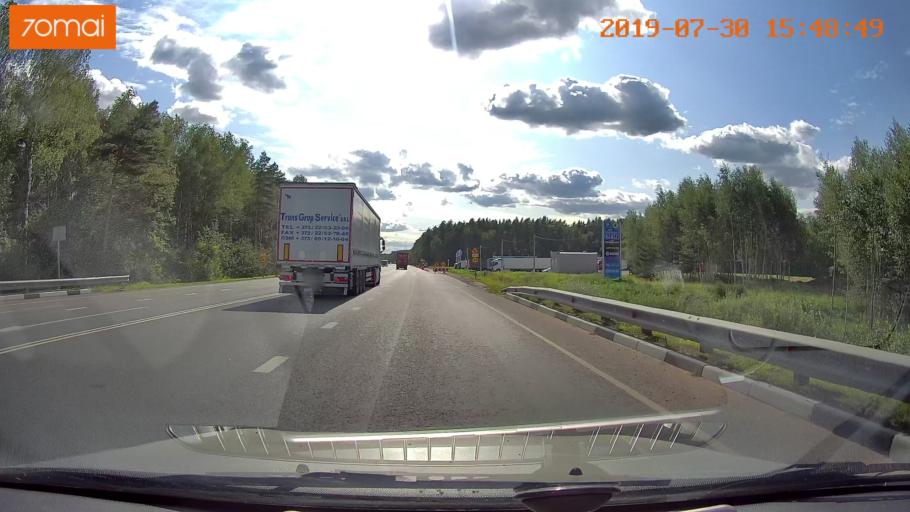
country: RU
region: Moskovskaya
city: Voskresensk
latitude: 55.3406
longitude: 38.6768
